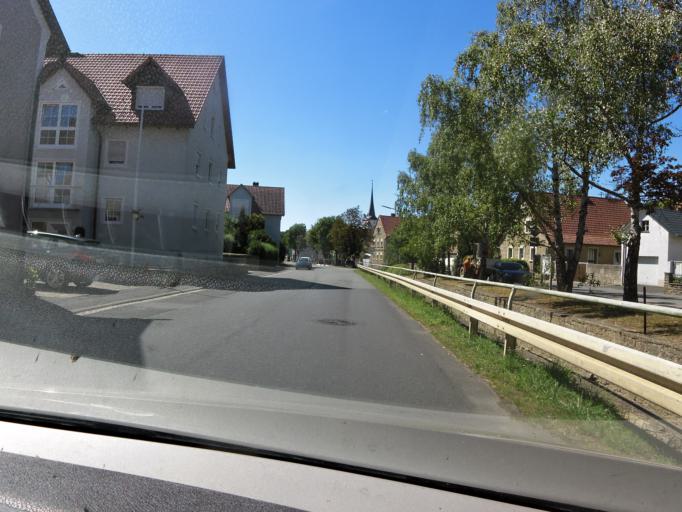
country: DE
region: Bavaria
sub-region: Regierungsbezirk Unterfranken
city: Theilheim
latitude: 49.7536
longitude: 10.0345
